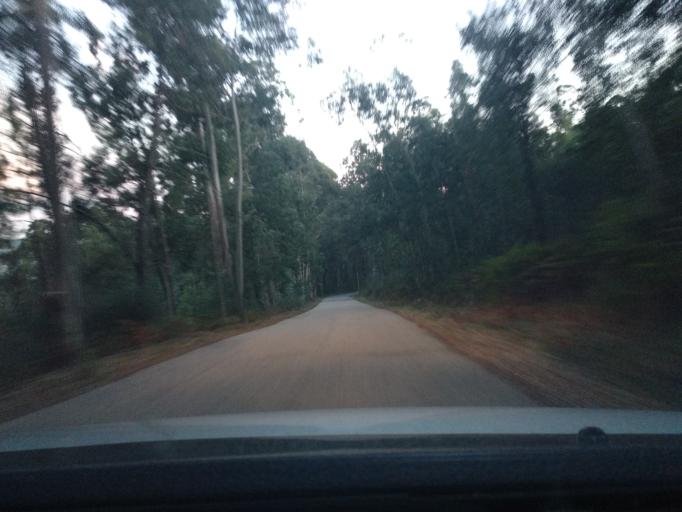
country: ES
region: Galicia
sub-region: Provincia de Pontevedra
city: Moana
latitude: 42.2988
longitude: -8.6951
